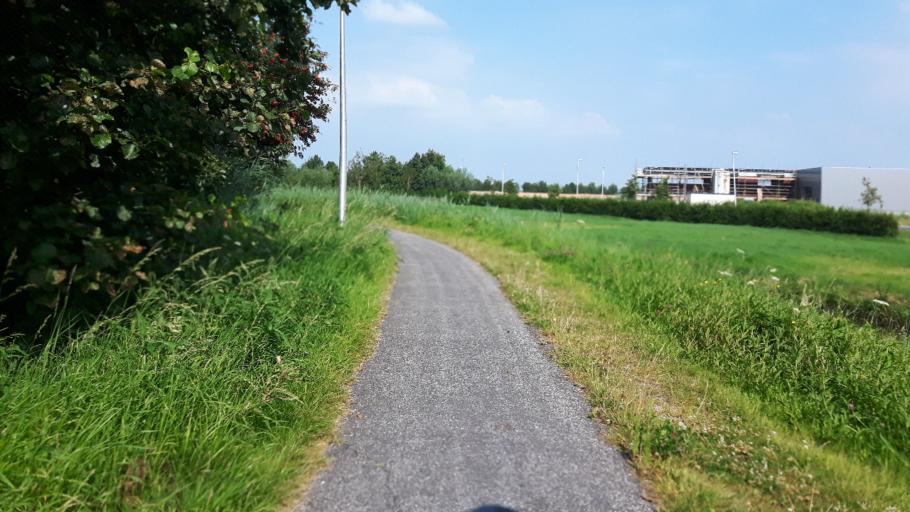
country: NL
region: South Holland
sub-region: Gemeente Schoonhoven
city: Schoonhoven
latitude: 51.9512
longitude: 4.8619
